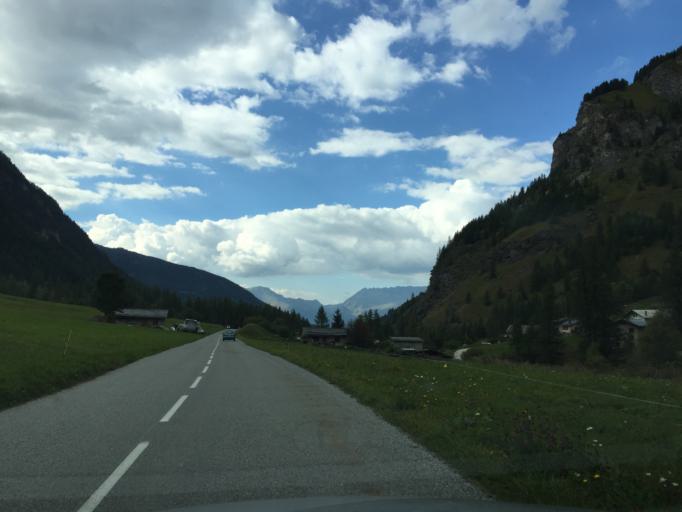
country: FR
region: Rhone-Alpes
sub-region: Departement de la Savoie
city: Belle-Plagne
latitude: 45.5228
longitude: 6.7953
